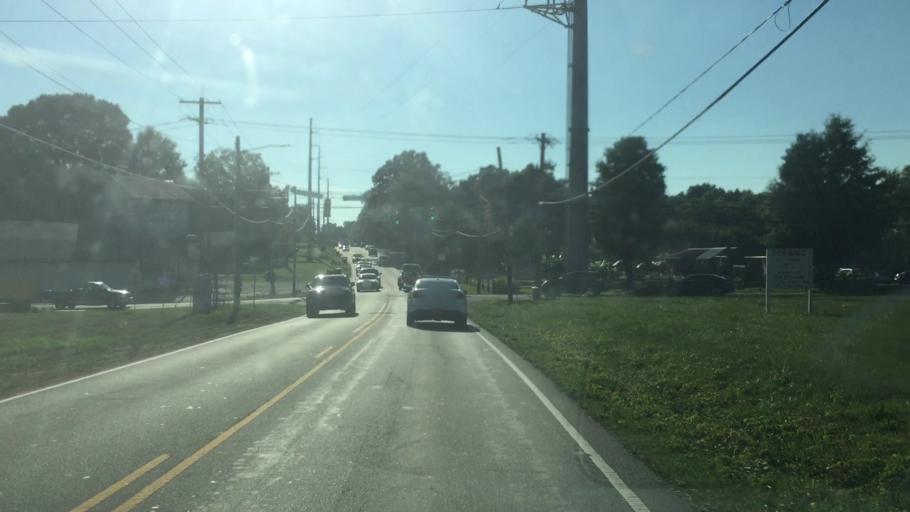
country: US
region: North Carolina
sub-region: Cabarrus County
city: Concord
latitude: 35.4130
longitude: -80.6386
